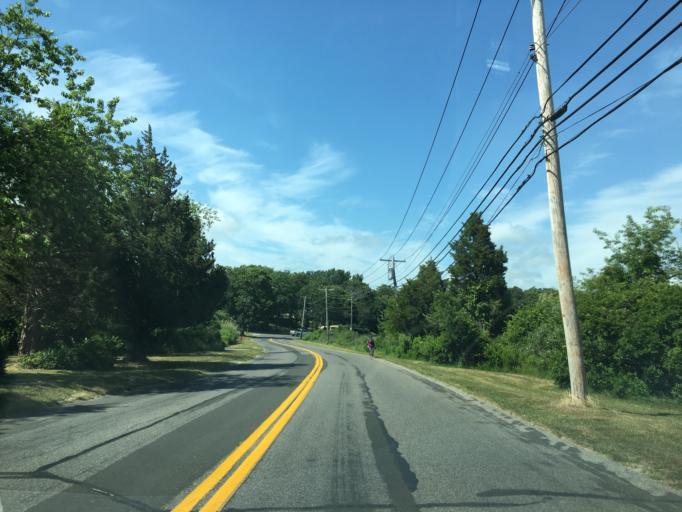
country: US
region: New York
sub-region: Suffolk County
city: Shelter Island Heights
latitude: 41.0613
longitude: -72.3677
